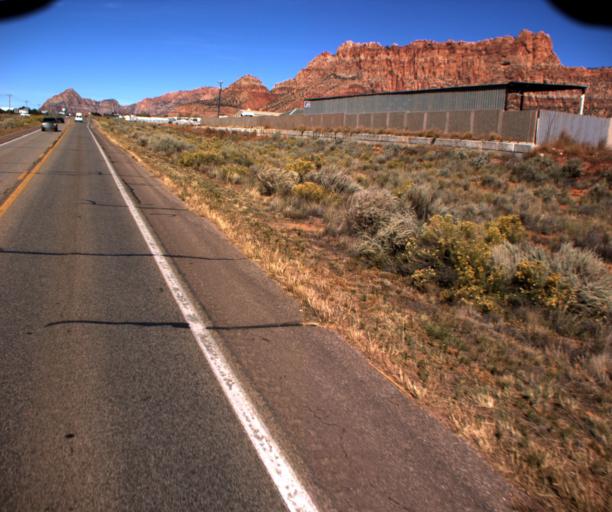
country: US
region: Arizona
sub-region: Mohave County
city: Colorado City
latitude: 36.9954
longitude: -112.9950
